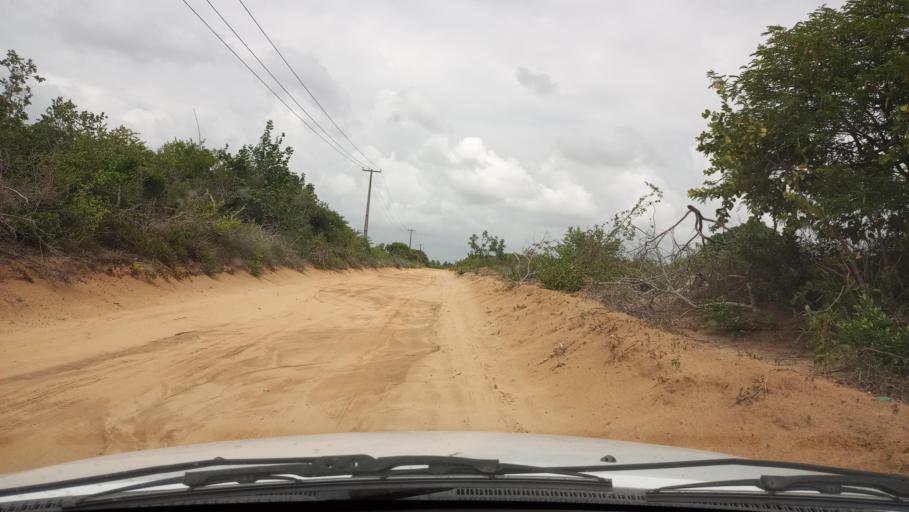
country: BR
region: Rio Grande do Norte
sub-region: Maxaranguape
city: Sao Miguel
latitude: -5.4838
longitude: -35.3075
